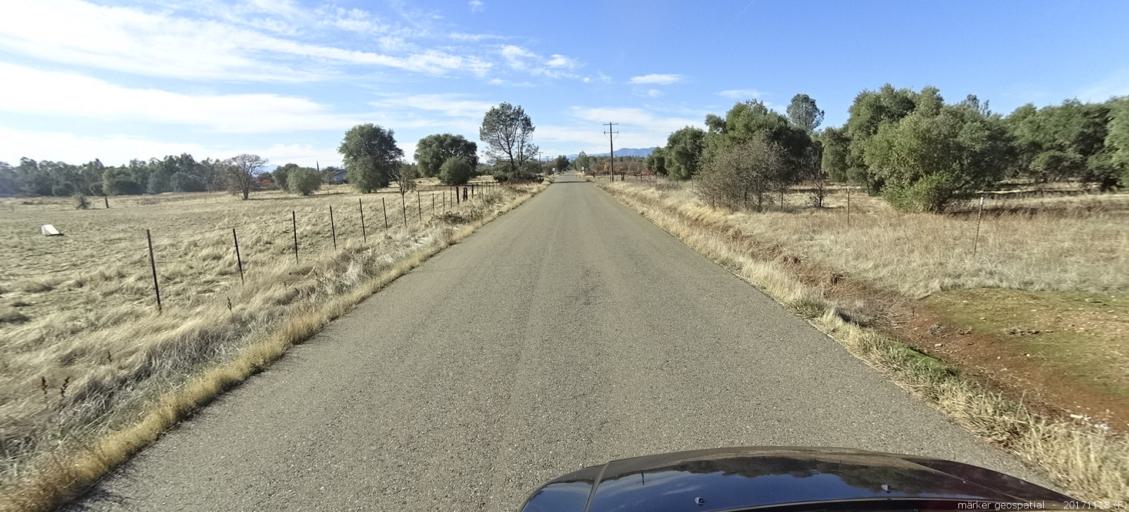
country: US
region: California
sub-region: Shasta County
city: Redding
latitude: 40.4562
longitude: -122.4418
